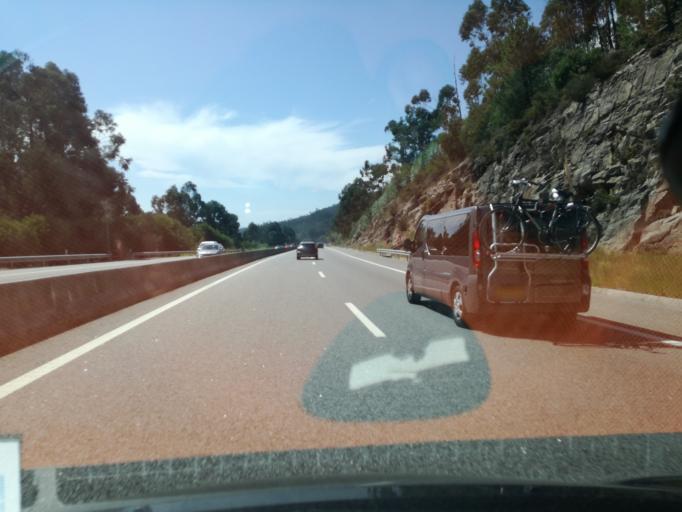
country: PT
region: Viana do Castelo
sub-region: Viana do Castelo
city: Meadela
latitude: 41.7570
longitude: -8.7957
